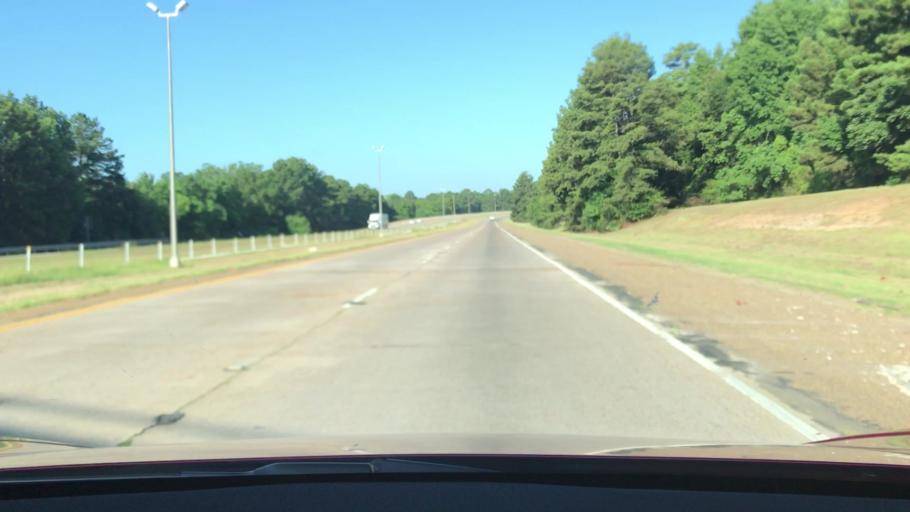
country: US
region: Louisiana
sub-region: Bossier Parish
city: Bossier City
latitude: 32.4179
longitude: -93.7805
